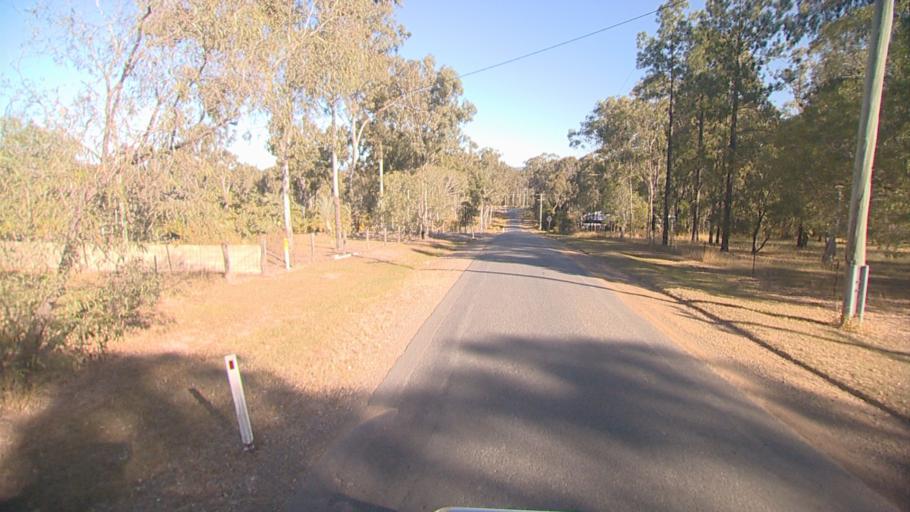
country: AU
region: Queensland
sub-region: Logan
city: North Maclean
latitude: -27.8083
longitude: 153.0336
